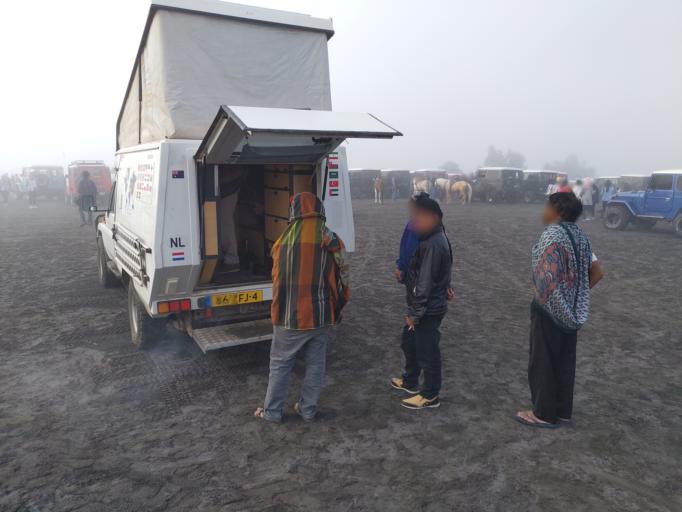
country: ID
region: East Java
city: Gubugklakah Barat
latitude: -7.9280
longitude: 112.9541
